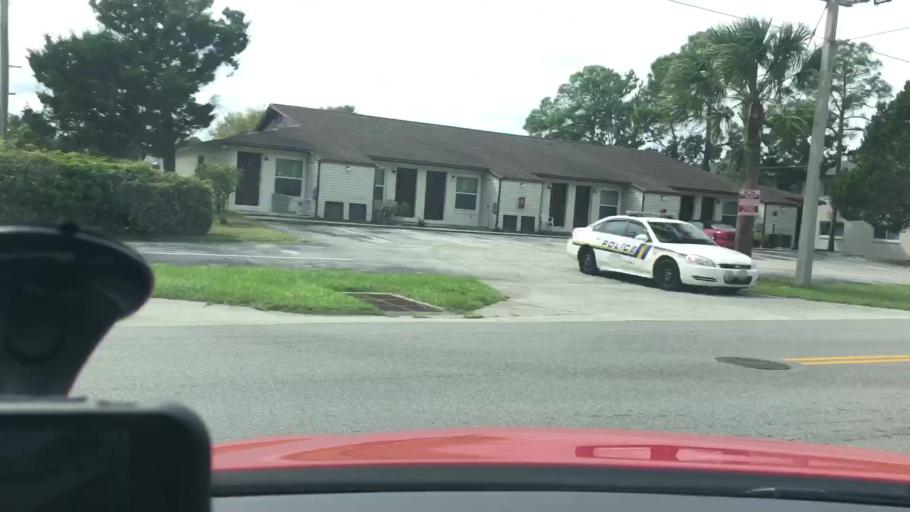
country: US
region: Florida
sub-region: Volusia County
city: South Daytona
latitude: 29.1755
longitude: -81.0021
